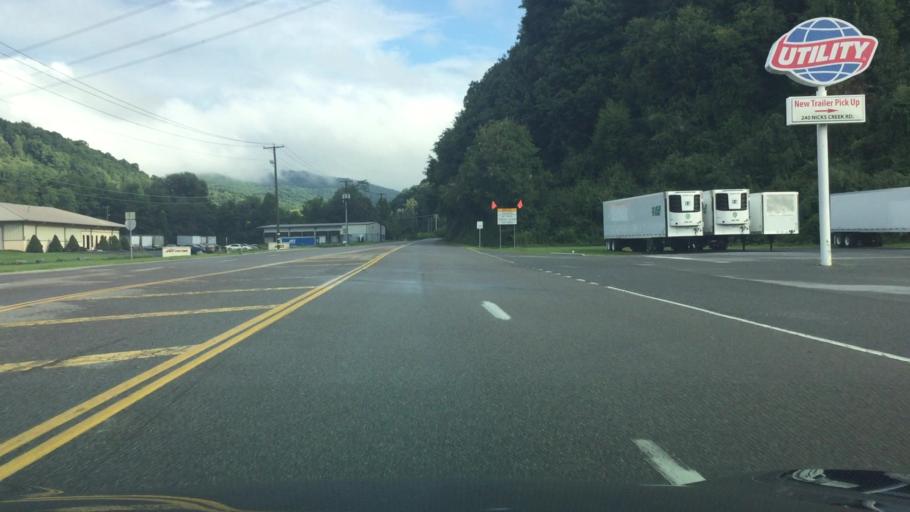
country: US
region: Virginia
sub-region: Smyth County
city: Atkins
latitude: 36.8609
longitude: -81.4329
